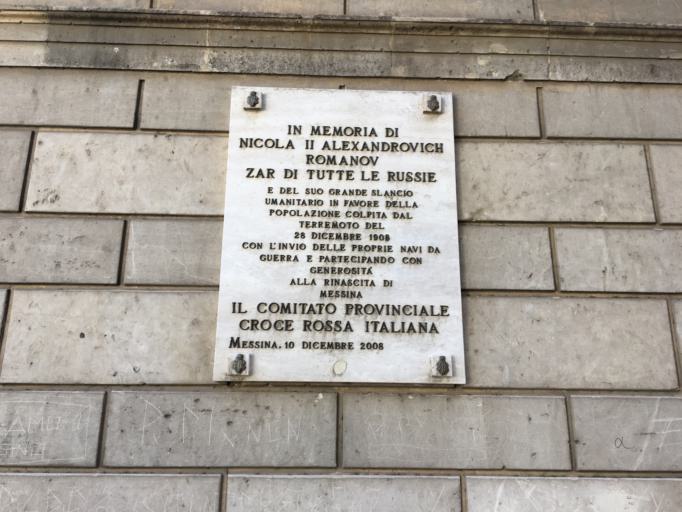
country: IT
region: Sicily
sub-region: Messina
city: Messina
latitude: 38.1958
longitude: 15.5567
